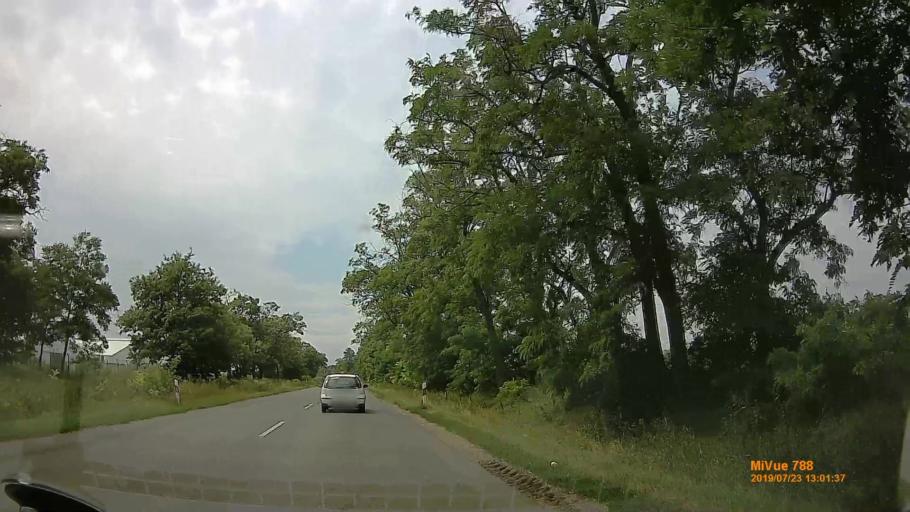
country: HU
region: Szabolcs-Szatmar-Bereg
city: Tiszavasvari
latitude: 47.9583
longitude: 21.4032
